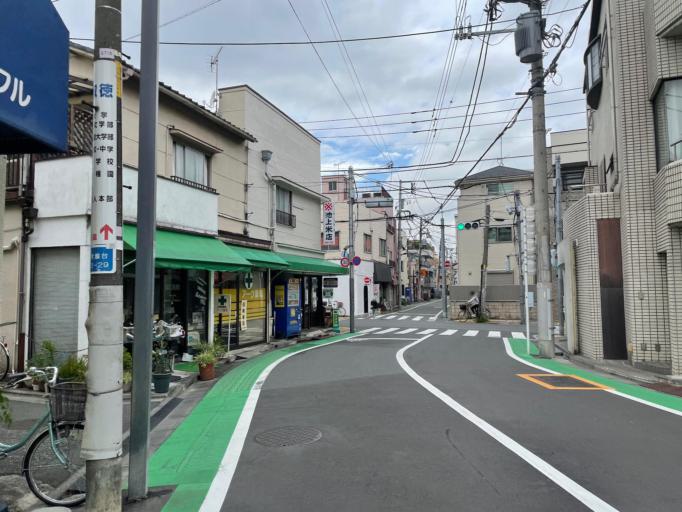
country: JP
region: Saitama
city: Kawaguchi
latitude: 35.7633
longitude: 139.6889
